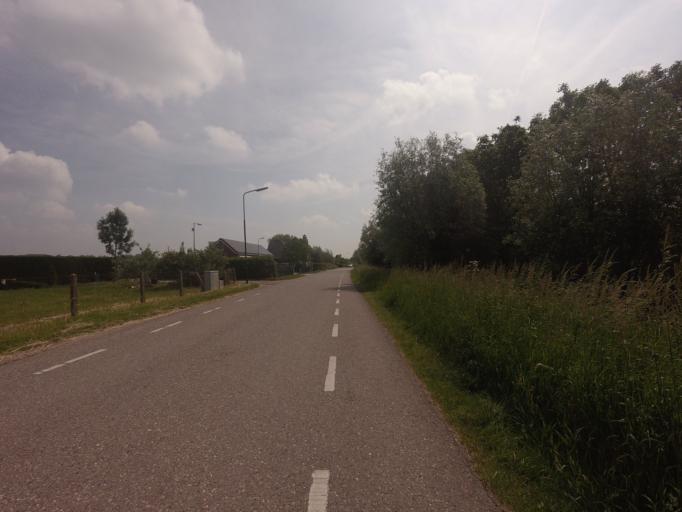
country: NL
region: Utrecht
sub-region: Gemeente Houten
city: Houten
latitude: 51.9975
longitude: 5.1484
